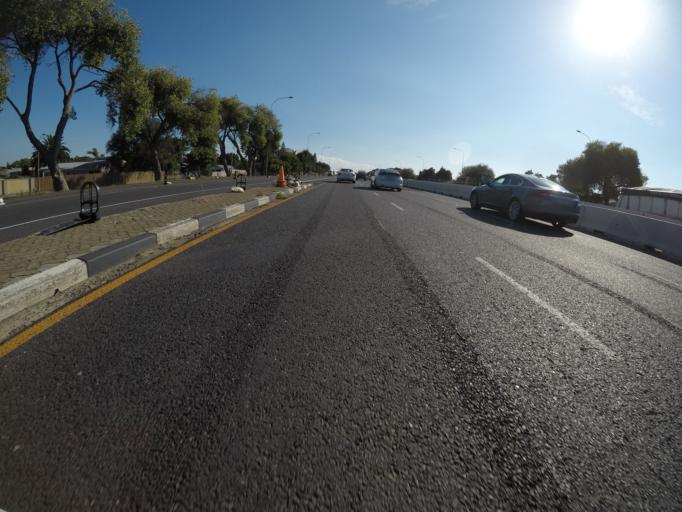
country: ZA
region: Western Cape
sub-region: City of Cape Town
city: Kraaifontein
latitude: -33.8786
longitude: 18.6553
